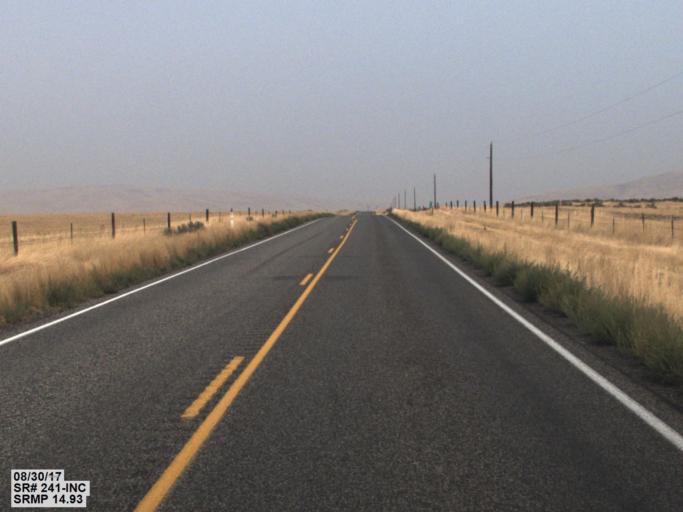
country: US
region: Washington
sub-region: Yakima County
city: Sunnyside
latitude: 46.4075
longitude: -119.9490
